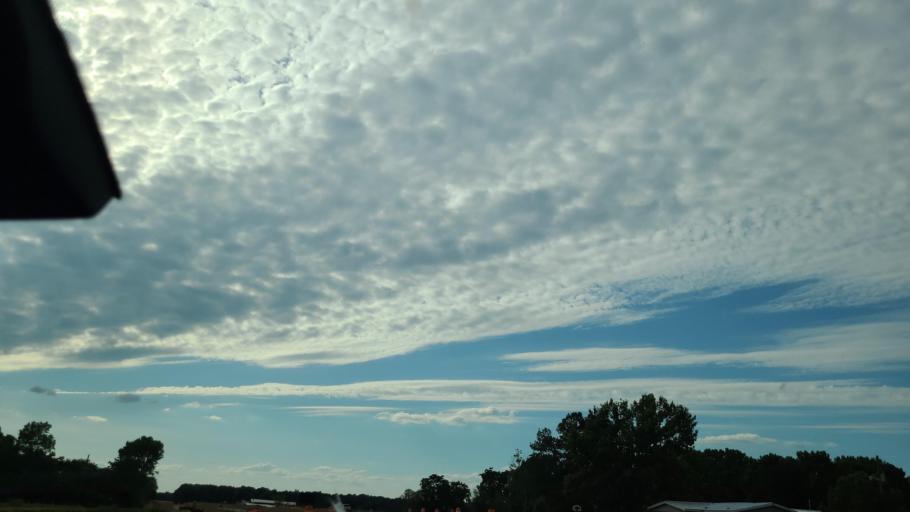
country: US
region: Georgia
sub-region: Putnam County
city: Jefferson
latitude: 33.4701
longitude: -83.4172
